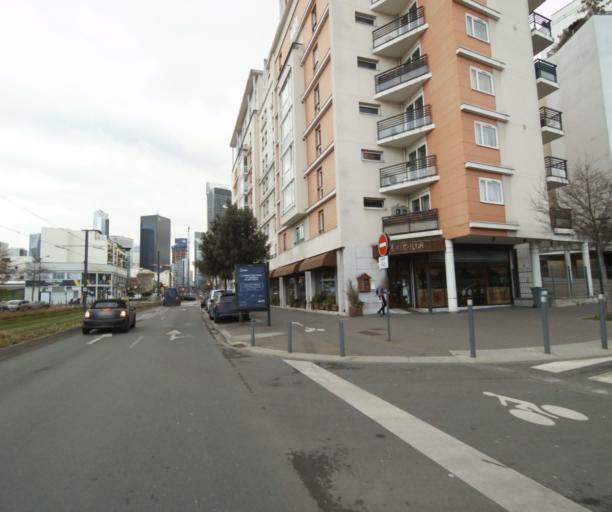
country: FR
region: Ile-de-France
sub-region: Departement des Hauts-de-Seine
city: La Garenne-Colombes
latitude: 48.9007
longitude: 2.2397
